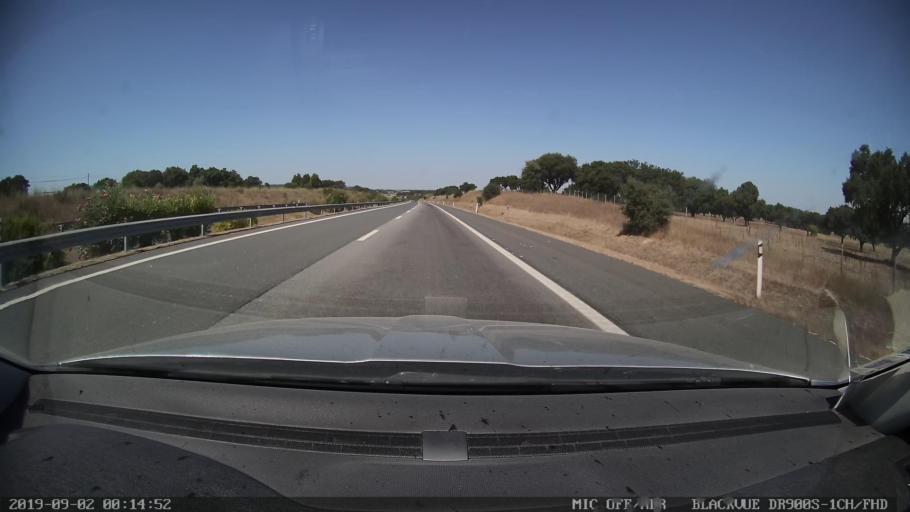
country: PT
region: Evora
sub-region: Arraiolos
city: Arraiolos
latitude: 38.6110
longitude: -8.0620
